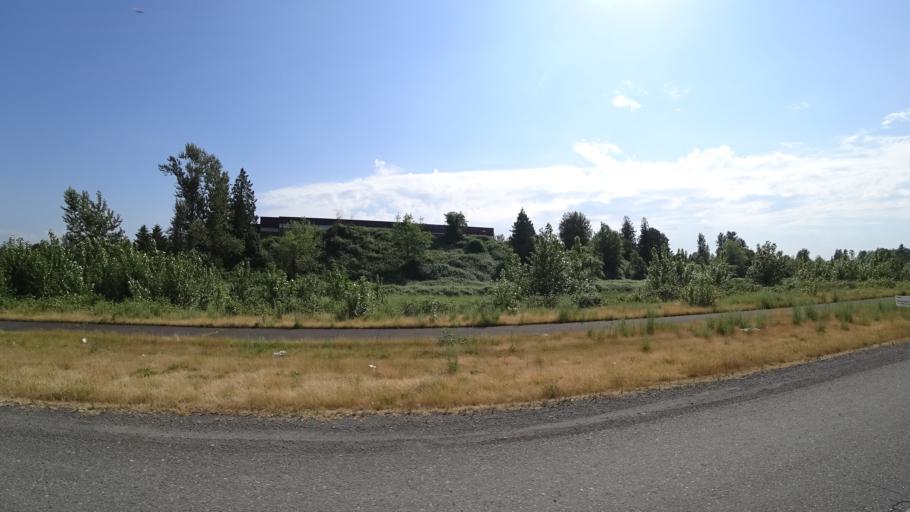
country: US
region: Oregon
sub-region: Multnomah County
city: Wood Village
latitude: 45.5484
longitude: -122.4164
